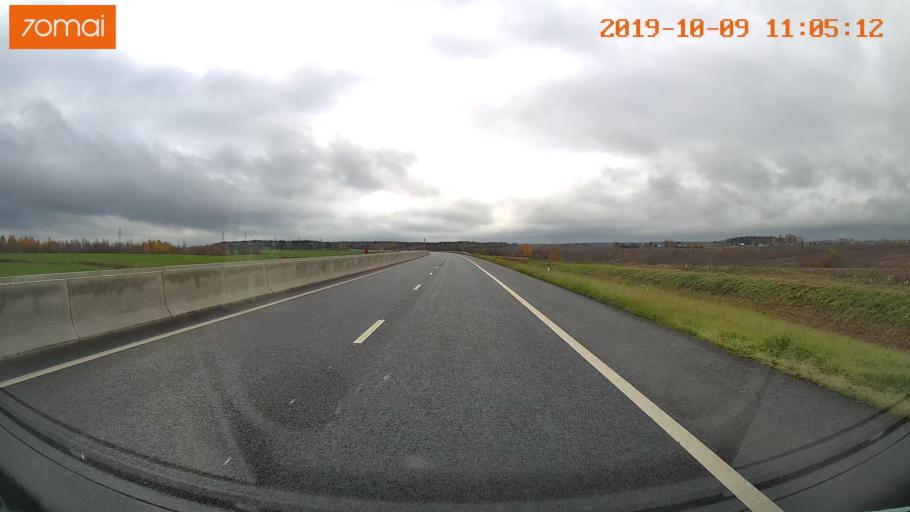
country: RU
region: Vologda
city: Molochnoye
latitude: 59.2031
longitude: 39.7598
